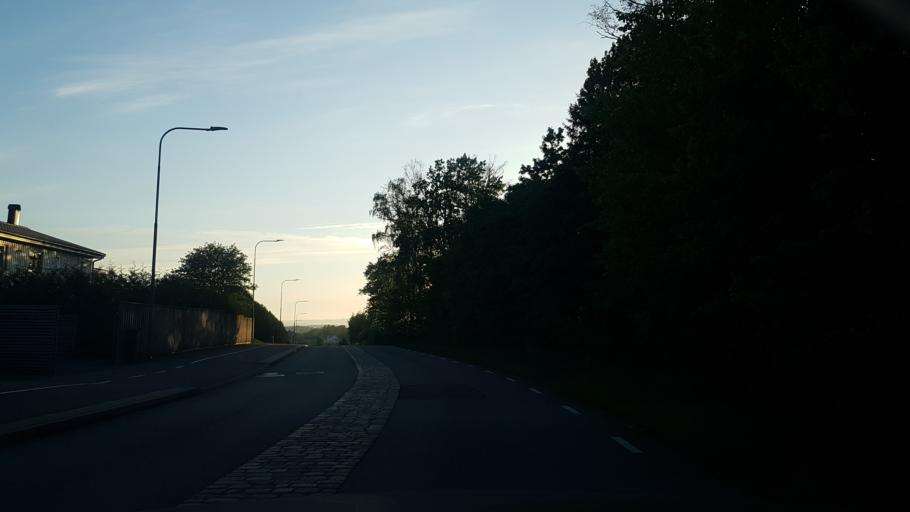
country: SE
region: Vaestra Goetaland
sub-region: Goteborg
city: Billdal
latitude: 57.5996
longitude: 11.9400
